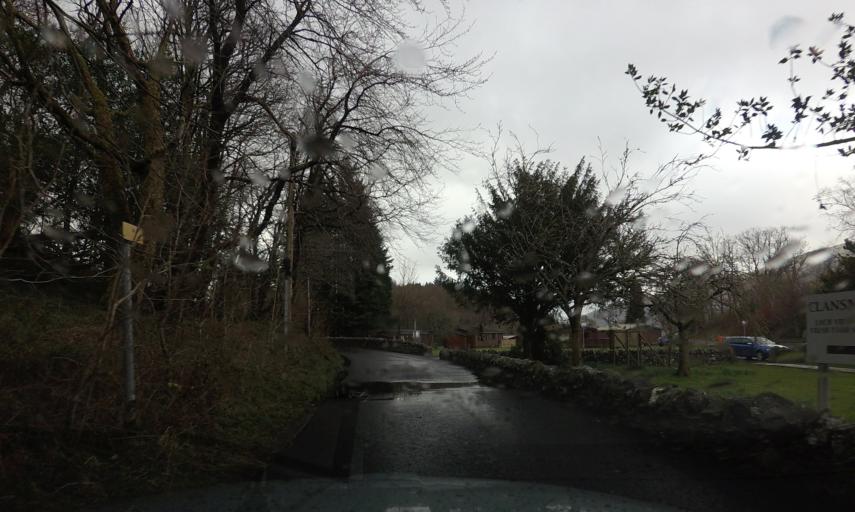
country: GB
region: Scotland
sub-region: West Dunbartonshire
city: Balloch
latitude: 56.1493
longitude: -4.6410
